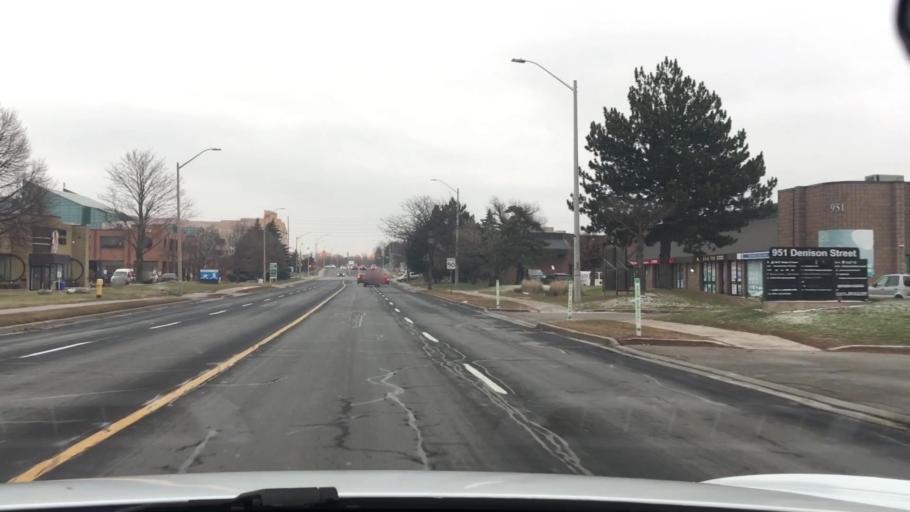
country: CA
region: Ontario
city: Markham
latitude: 43.8264
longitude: -79.3307
